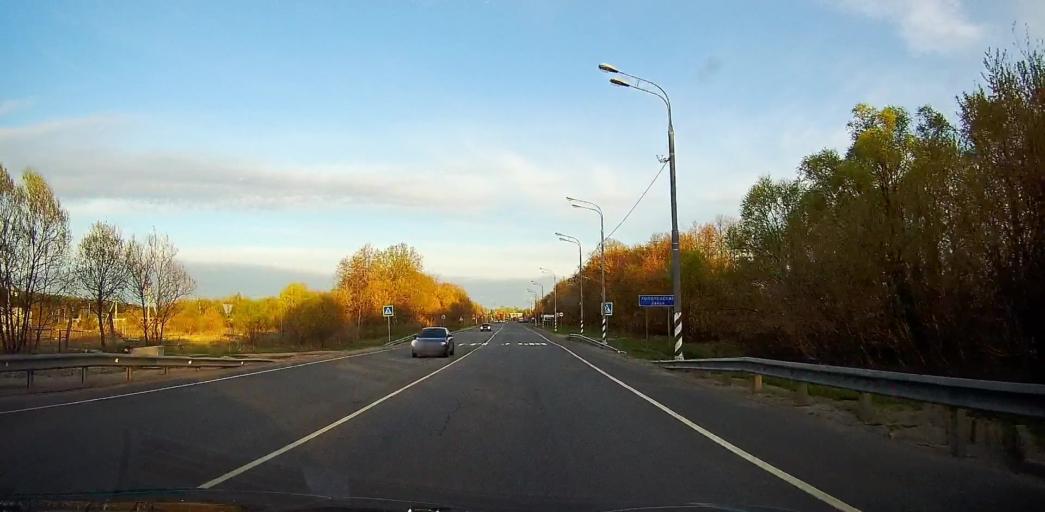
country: RU
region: Moskovskaya
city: Troitskoye
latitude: 55.2303
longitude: 38.5542
